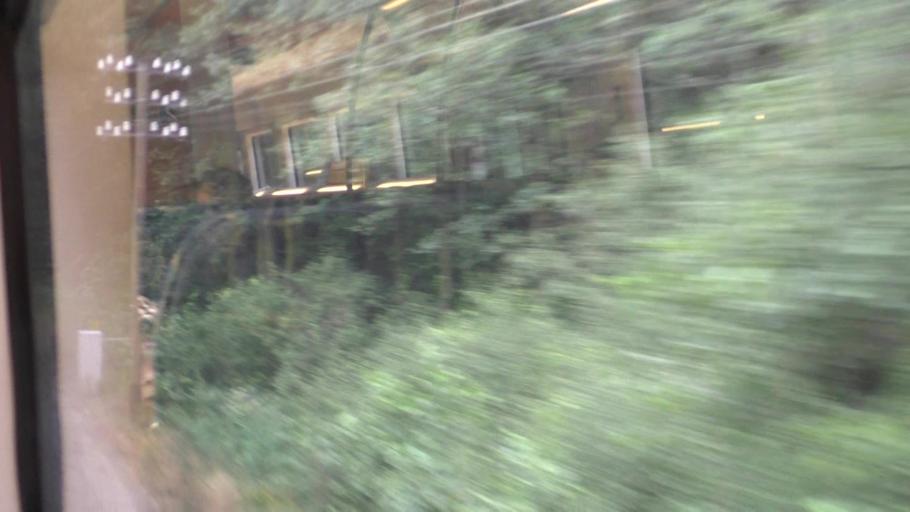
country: DE
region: Saxony
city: Horka
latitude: 51.2716
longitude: 14.9072
